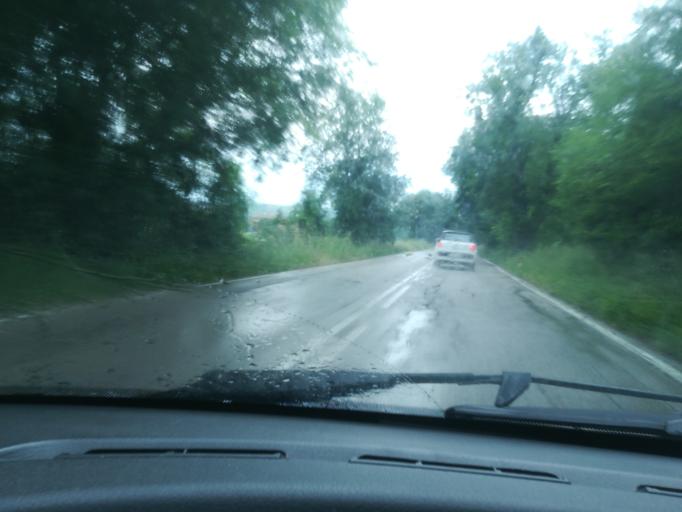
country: IT
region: The Marches
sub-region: Provincia di Macerata
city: Pollenza
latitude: 43.2881
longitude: 13.3814
